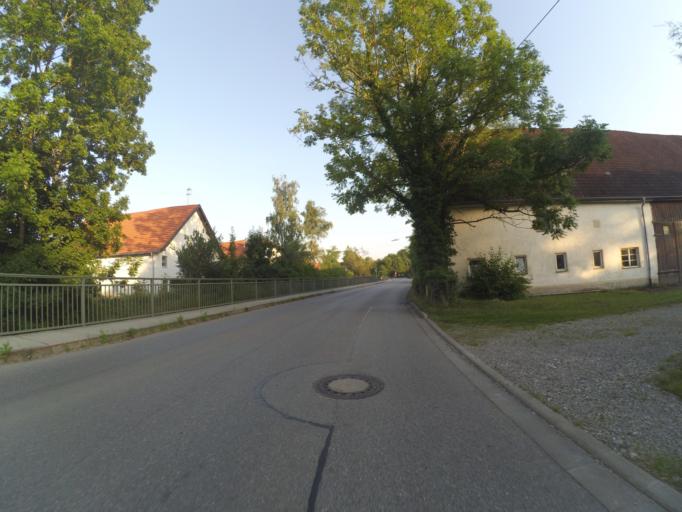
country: DE
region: Bavaria
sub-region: Swabia
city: Jengen
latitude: 48.0018
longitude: 10.7250
